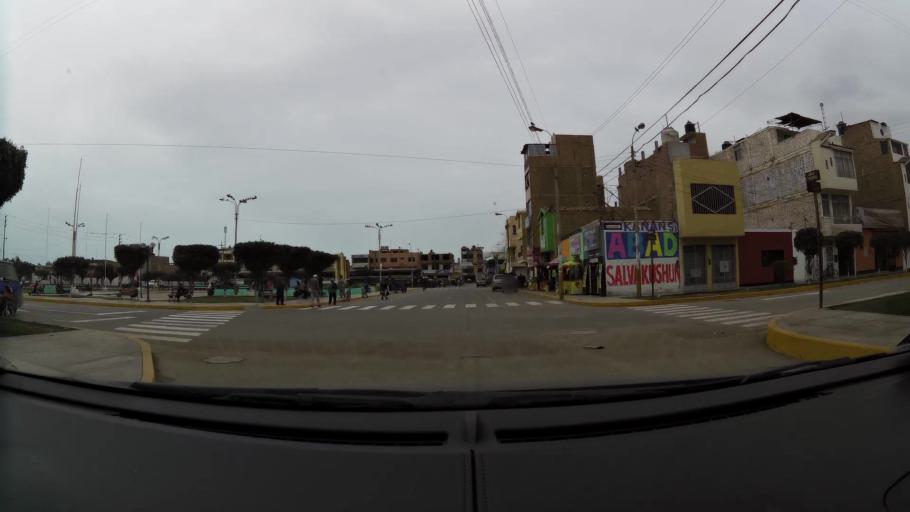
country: PE
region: Lima
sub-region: Barranca
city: Paramonga
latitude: -10.6740
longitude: -77.8182
